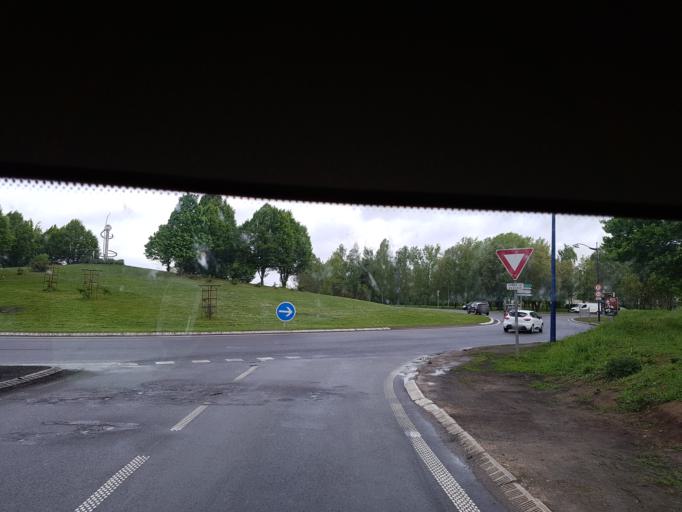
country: FR
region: Picardie
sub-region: Departement de l'Aisne
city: Courmelles
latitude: 49.3659
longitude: 3.3109
